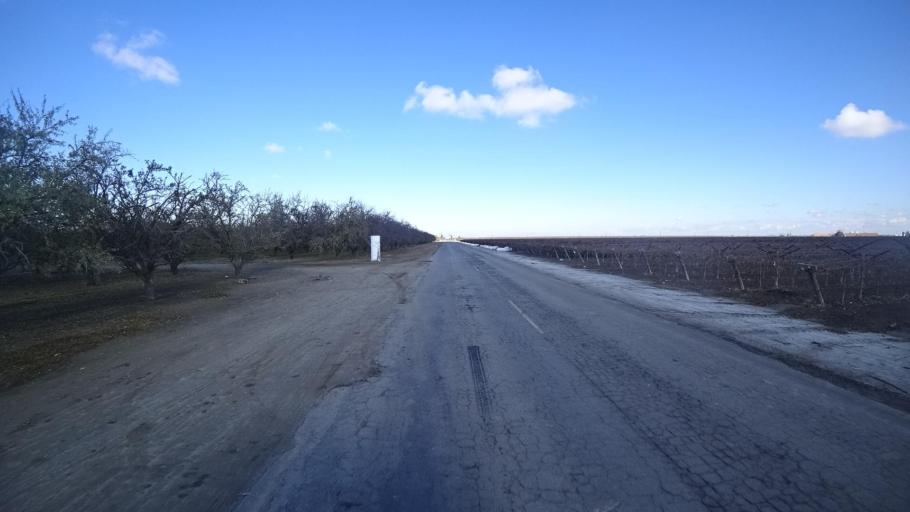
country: US
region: California
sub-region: Kern County
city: McFarland
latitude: 35.6850
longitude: -119.2587
